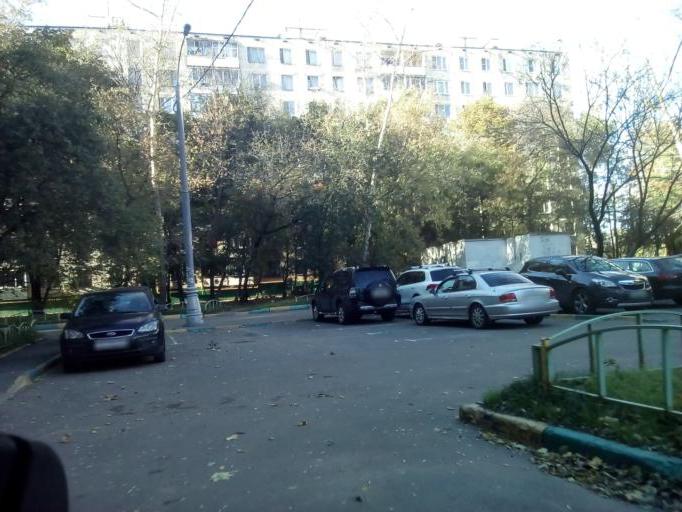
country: RU
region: Moscow
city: Likhobory
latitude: 55.8459
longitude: 37.5557
